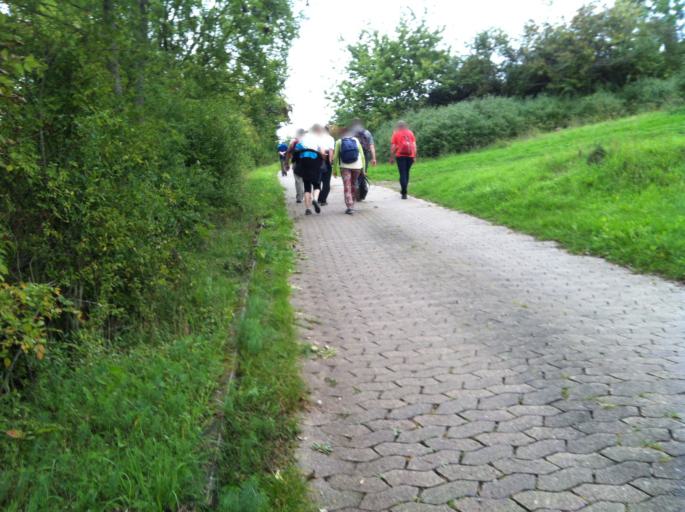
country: DE
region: Thuringia
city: Bornhagen
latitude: 51.3312
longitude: 9.9232
